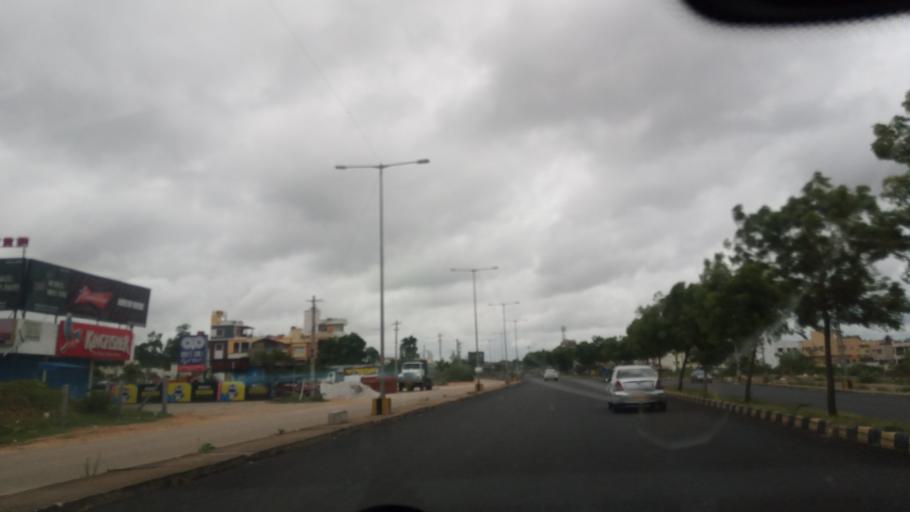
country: IN
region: Karnataka
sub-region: Mysore
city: Mysore
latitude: 12.3278
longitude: 76.5973
